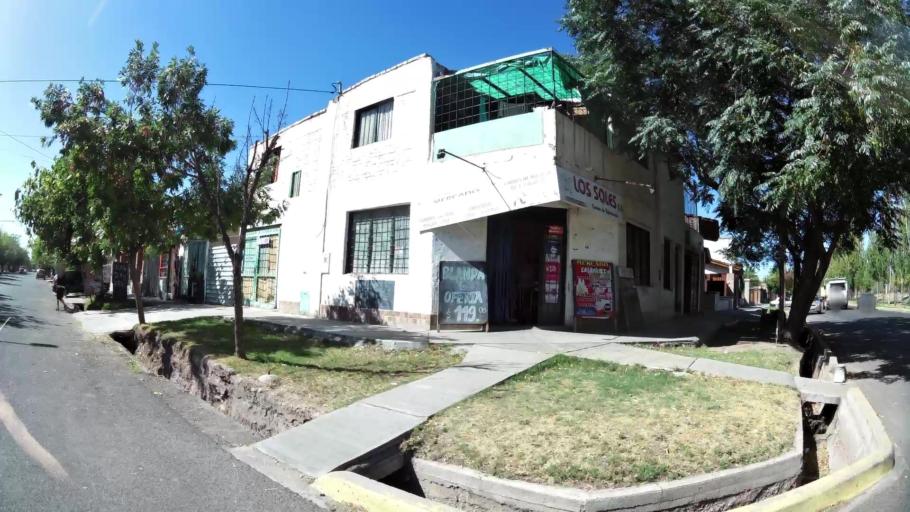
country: AR
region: Mendoza
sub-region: Departamento de Maipu
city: Maipu
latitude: -32.9719
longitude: -68.7997
